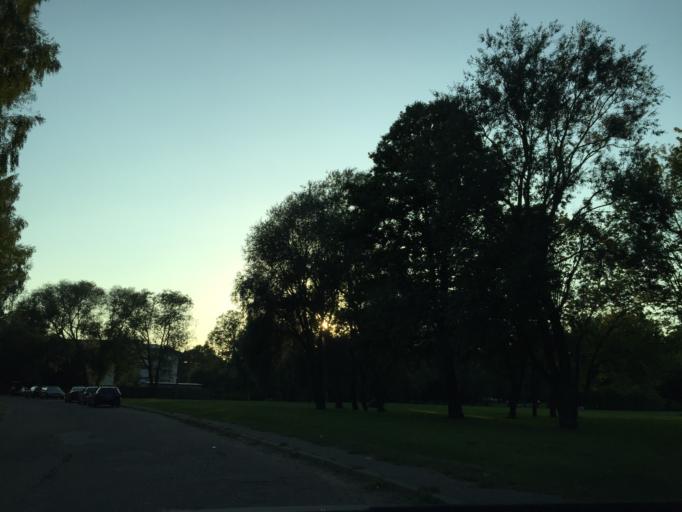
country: LV
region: Riga
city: Riga
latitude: 56.9611
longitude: 24.0599
